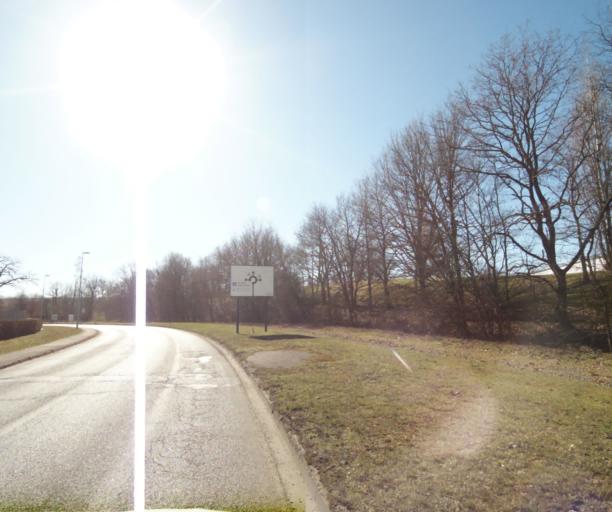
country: FR
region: Lorraine
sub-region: Departement de Meurthe-et-Moselle
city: Fleville-devant-Nancy
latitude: 48.6117
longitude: 6.1907
